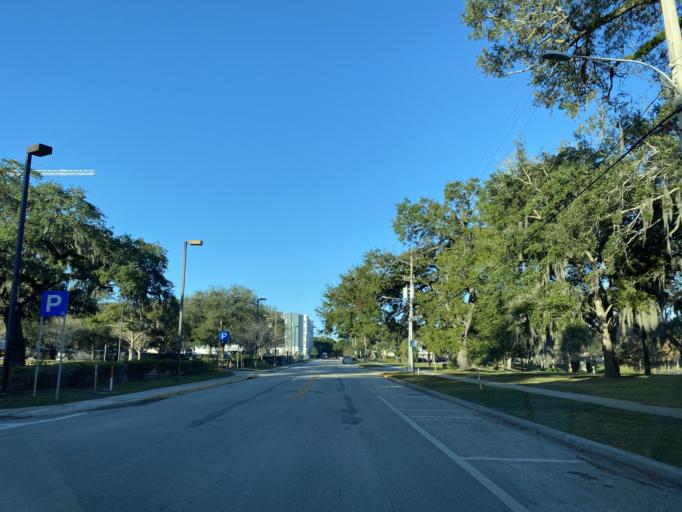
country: US
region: Florida
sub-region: Orange County
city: Orlando
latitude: 28.5509
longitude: -81.3854
